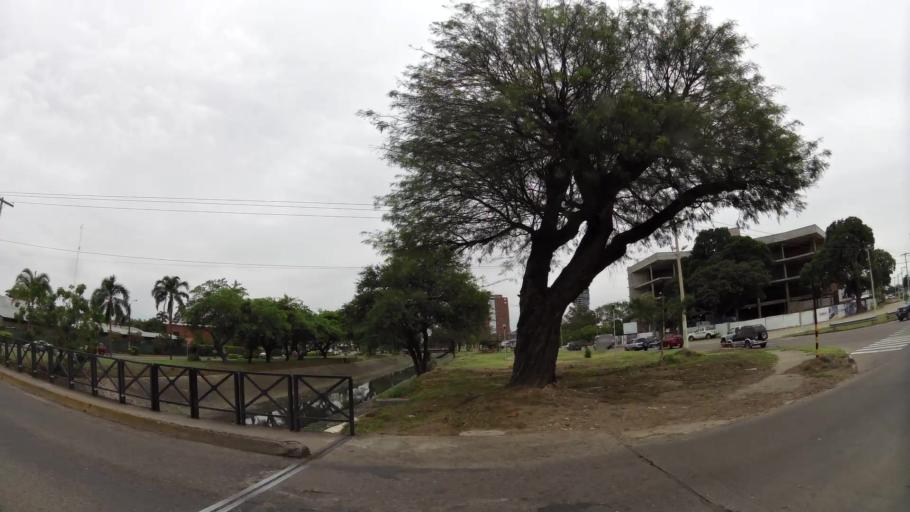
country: BO
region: Santa Cruz
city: Santa Cruz de la Sierra
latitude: -17.7603
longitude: -63.1915
